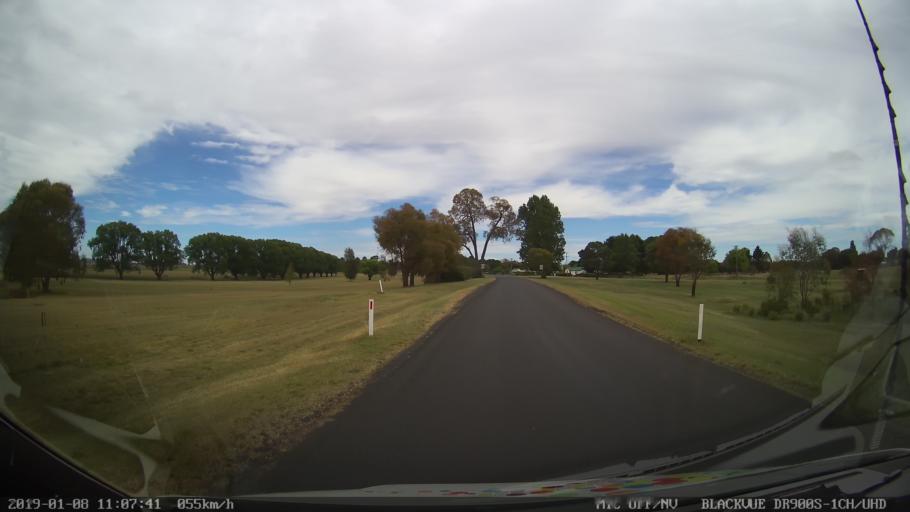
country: AU
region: New South Wales
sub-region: Guyra
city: Guyra
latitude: -30.2173
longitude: 151.6634
